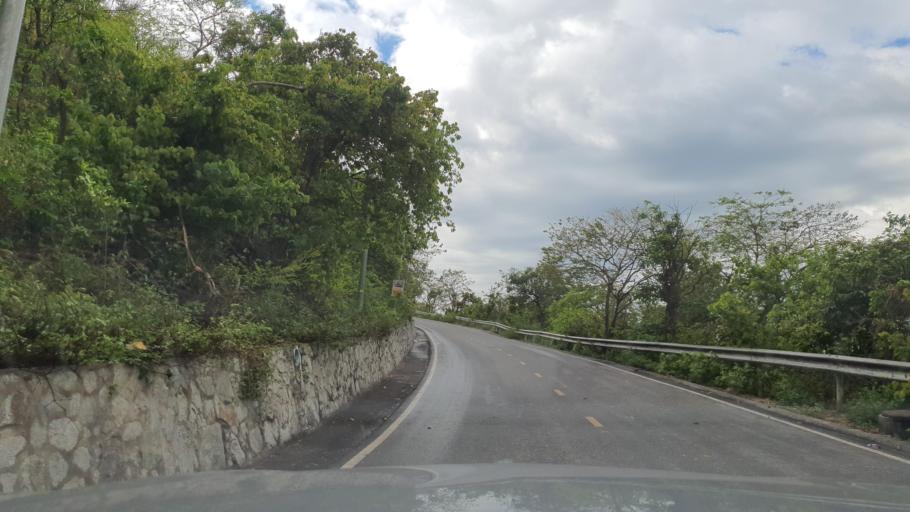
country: TH
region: Chon Buri
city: Chon Buri
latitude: 13.3110
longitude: 100.9040
